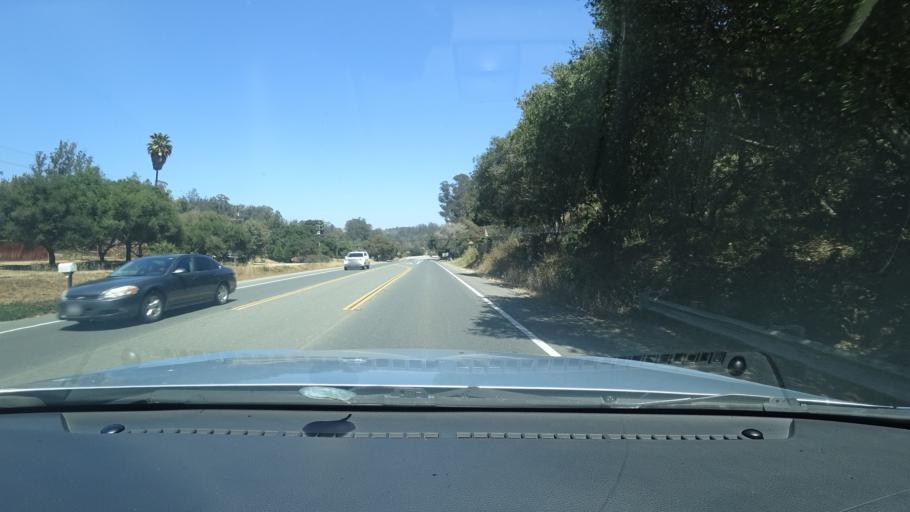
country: US
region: California
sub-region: Monterey County
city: Prunedale
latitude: 36.7884
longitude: -121.6766
